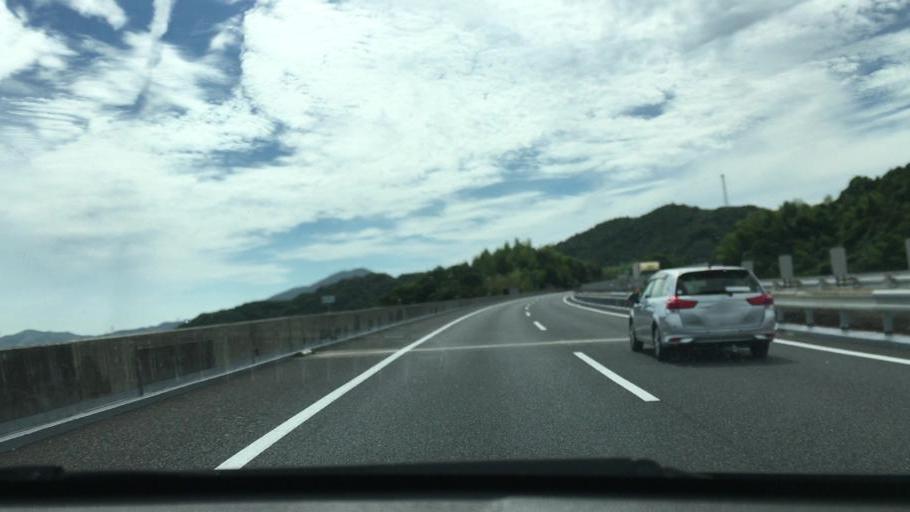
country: JP
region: Yamaguchi
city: Hofu
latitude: 34.0508
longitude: 131.5173
